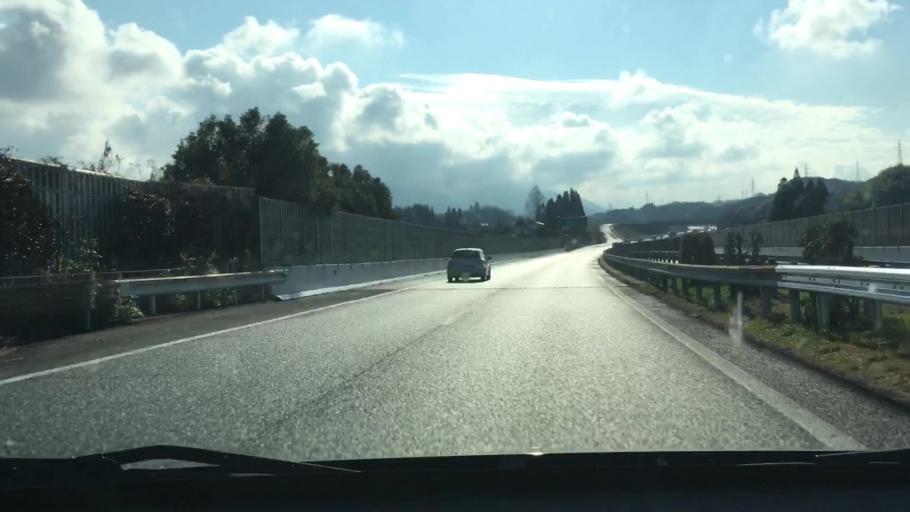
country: JP
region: Kumamoto
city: Matsubase
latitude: 32.5812
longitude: 130.7145
